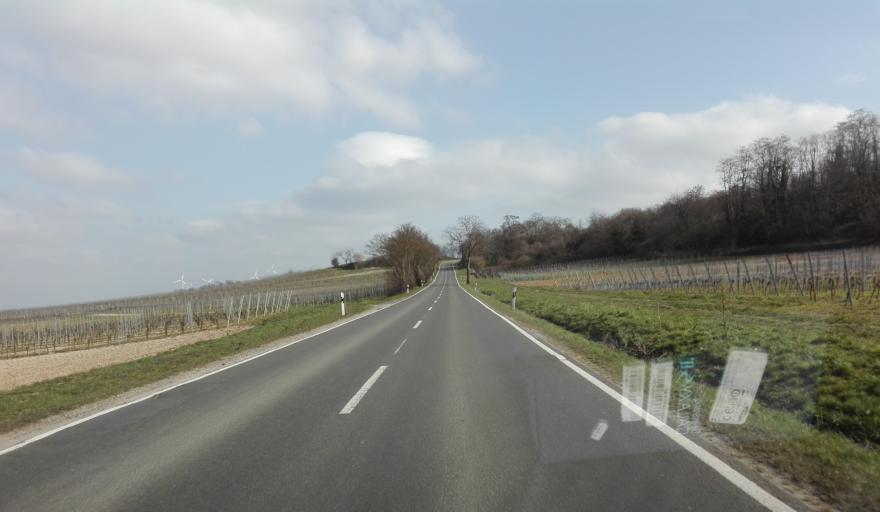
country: DE
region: Rheinland-Pfalz
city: Monsheim
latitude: 49.6524
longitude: 8.2284
